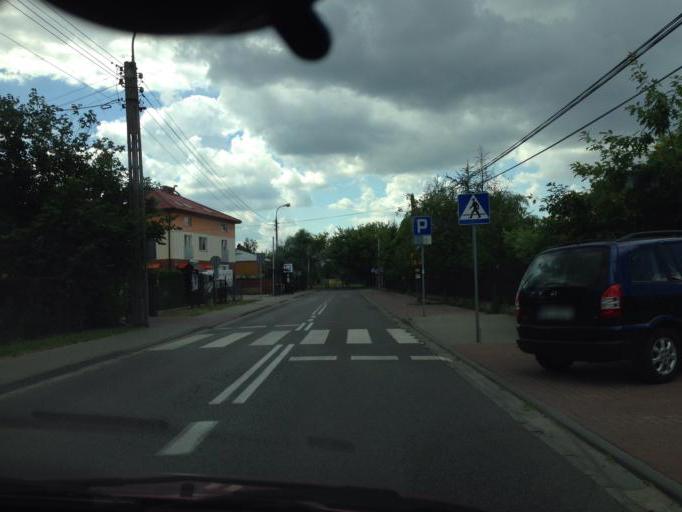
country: PL
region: Masovian Voivodeship
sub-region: Warszawa
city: Bemowo
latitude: 52.2444
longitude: 20.8833
